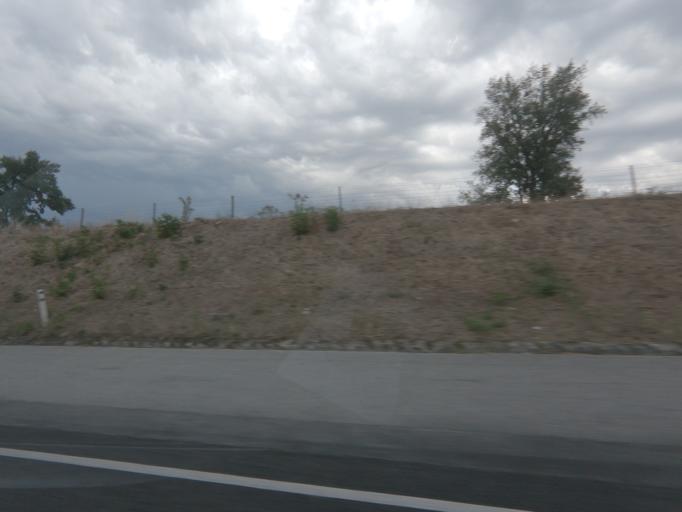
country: PT
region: Viseu
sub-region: Lamego
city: Lamego
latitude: 41.0930
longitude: -7.7826
